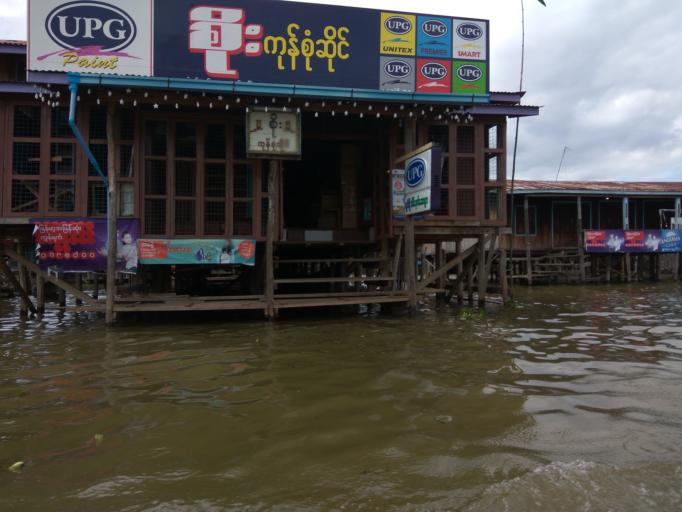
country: MM
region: Shan
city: Taunggyi
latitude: 20.4577
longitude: 96.9069
